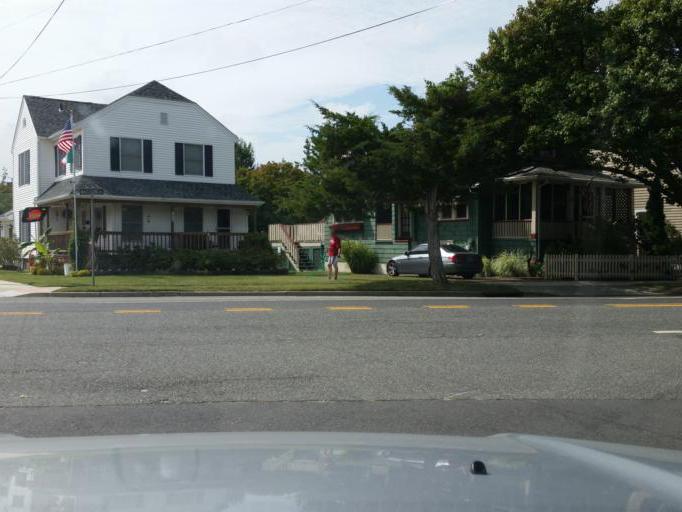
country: US
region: New Jersey
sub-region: Cape May County
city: Cape May
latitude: 38.9360
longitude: -74.9137
